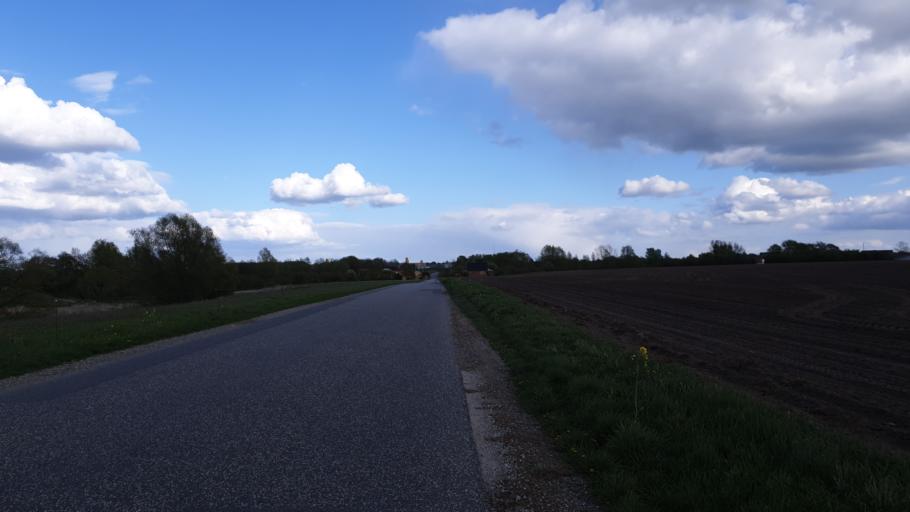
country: DK
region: Central Jutland
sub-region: Hedensted Kommune
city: Hedensted
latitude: 55.8116
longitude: 9.6633
